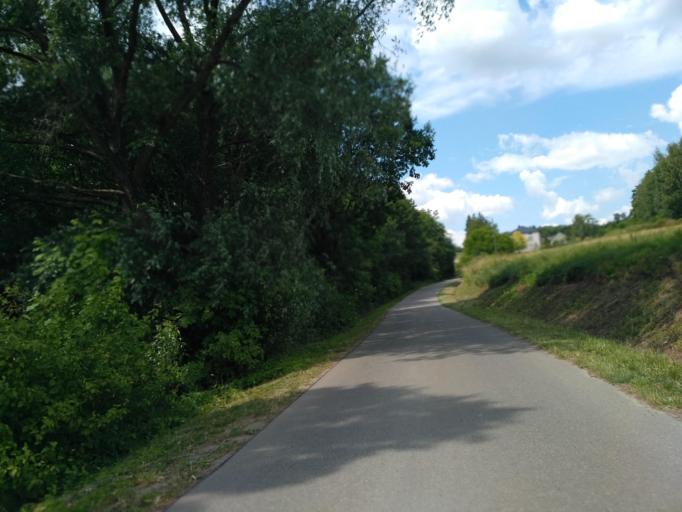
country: PL
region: Subcarpathian Voivodeship
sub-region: Powiat jasielski
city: Brzyska
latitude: 49.8024
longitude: 21.3996
